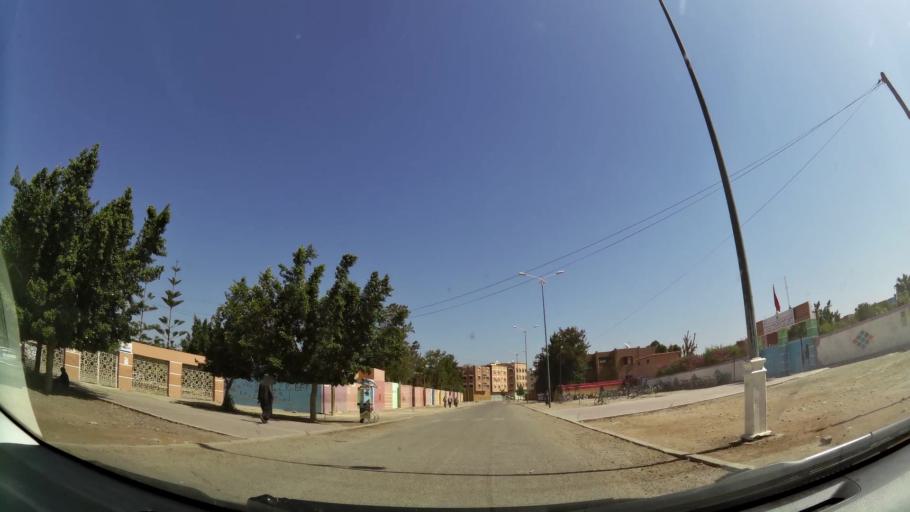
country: MA
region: Souss-Massa-Draa
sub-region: Inezgane-Ait Mellou
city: Inezgane
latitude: 30.3273
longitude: -9.5071
